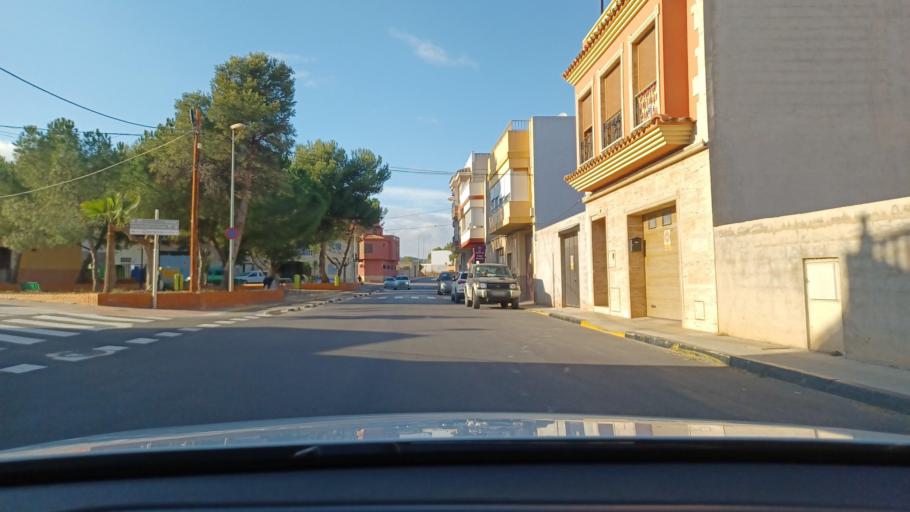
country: ES
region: Valencia
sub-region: Provincia de Castello
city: Betxi
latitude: 39.9313
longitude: -0.2002
